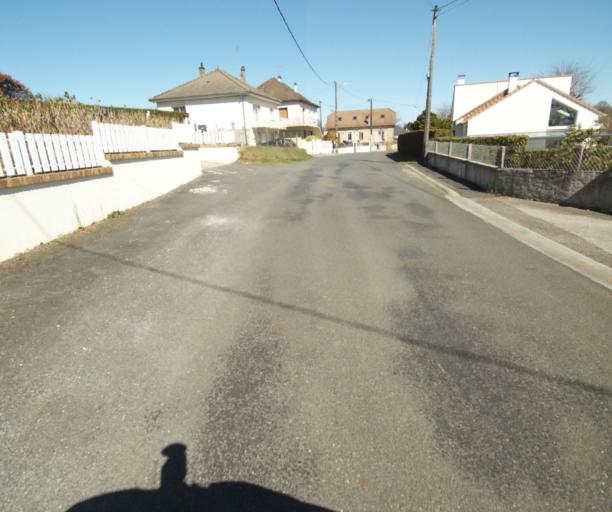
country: FR
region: Limousin
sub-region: Departement de la Correze
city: Seilhac
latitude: 45.3644
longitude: 1.7188
